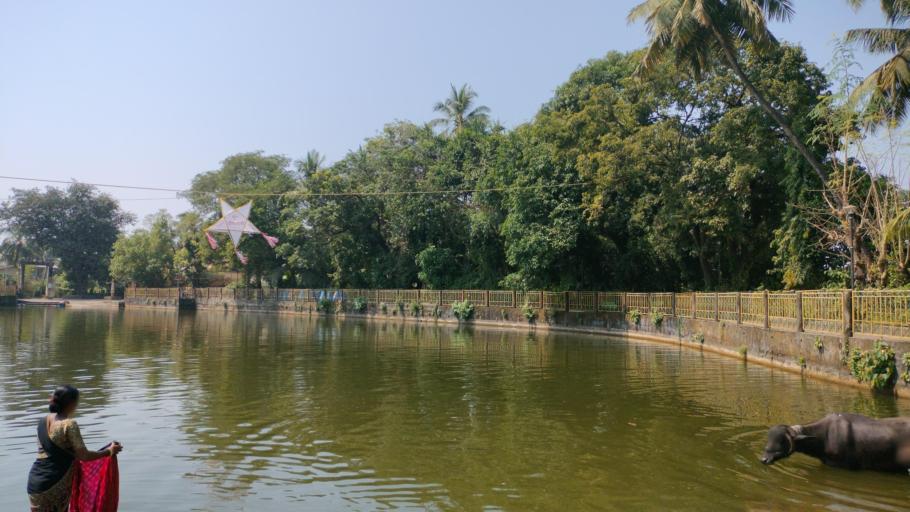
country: IN
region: Maharashtra
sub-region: Thane
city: Bhayandar
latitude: 19.3581
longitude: 72.8350
